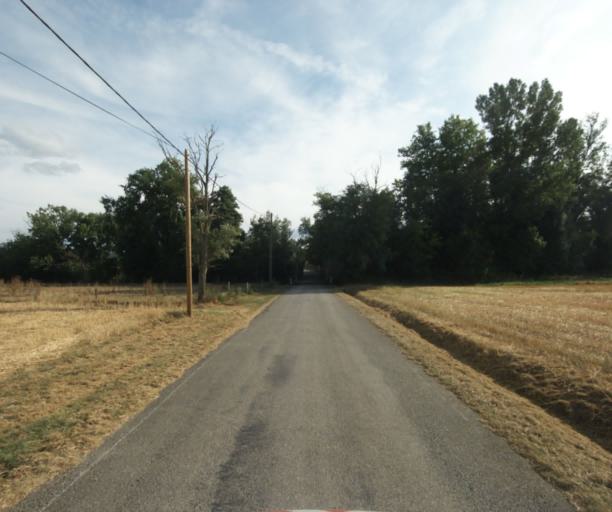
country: FR
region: Midi-Pyrenees
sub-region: Departement de la Haute-Garonne
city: Revel
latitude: 43.4723
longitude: 1.9979
